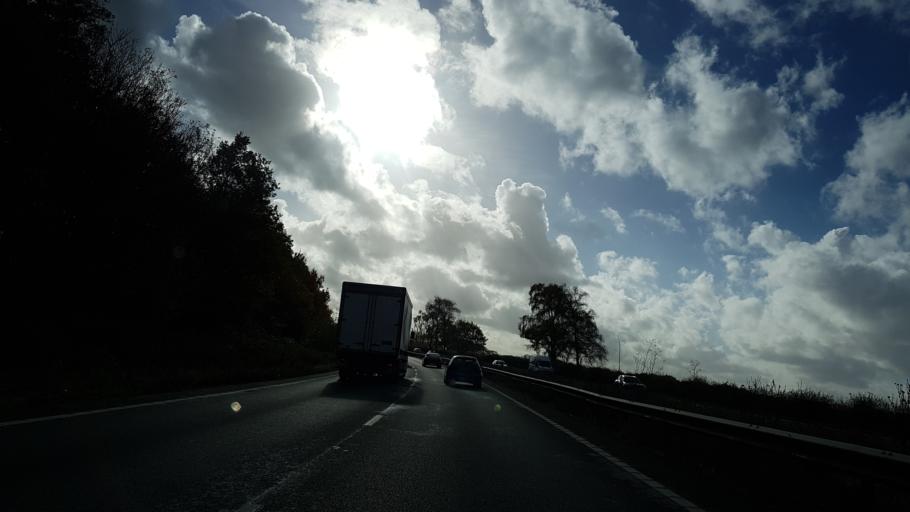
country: GB
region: England
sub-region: Surrey
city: Milford
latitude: 51.2053
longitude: -0.6506
